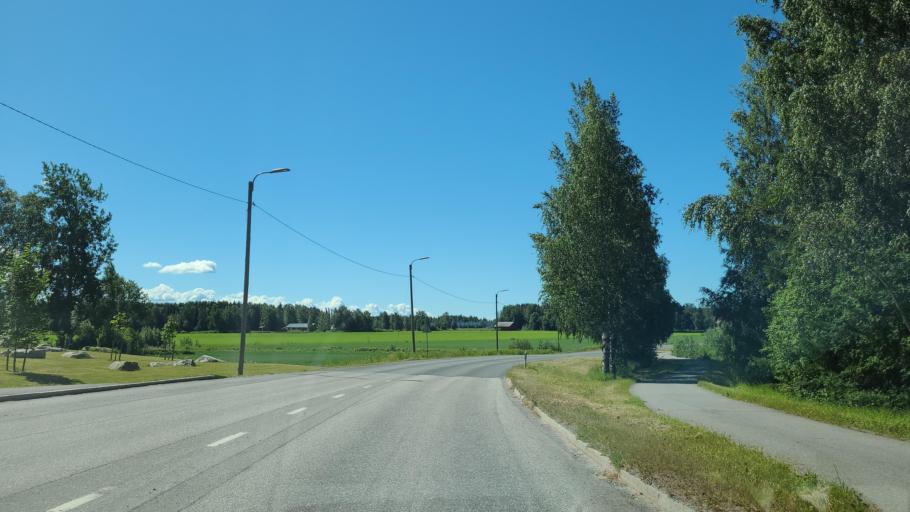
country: FI
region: Ostrobothnia
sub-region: Vaasa
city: Ristinummi
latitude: 63.0567
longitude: 21.7307
